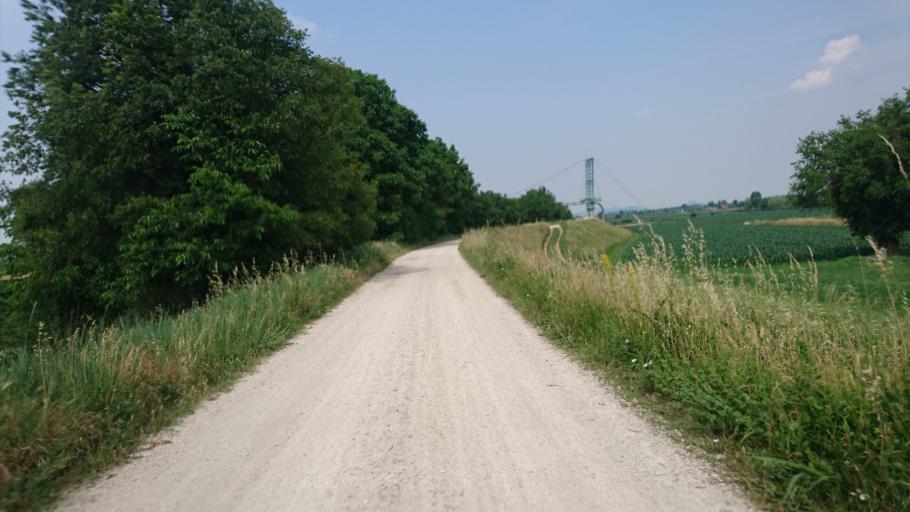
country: IT
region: Veneto
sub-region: Provincia di Padova
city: Terrassa Padovana
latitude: 45.2796
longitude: 11.8963
